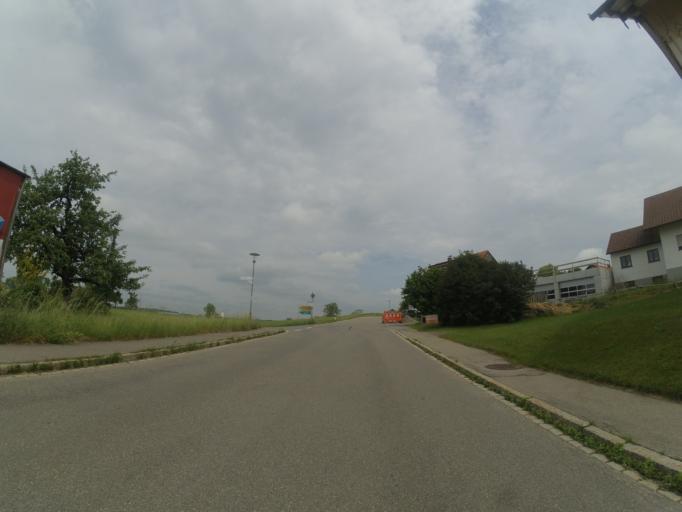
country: DE
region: Baden-Wuerttemberg
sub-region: Tuebingen Region
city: Isny im Allgau
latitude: 47.7443
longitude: 10.0129
